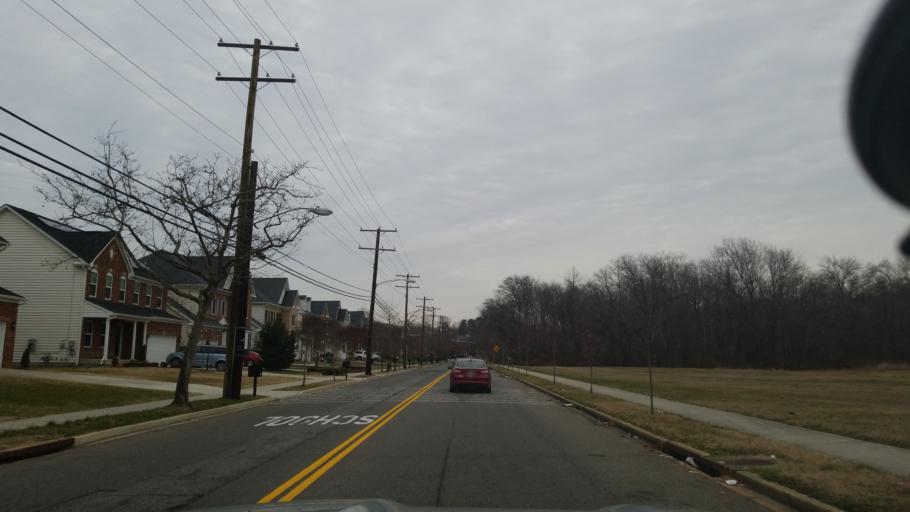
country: US
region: Maryland
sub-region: Prince George's County
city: Hillcrest Heights
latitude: 38.8419
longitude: -76.9820
